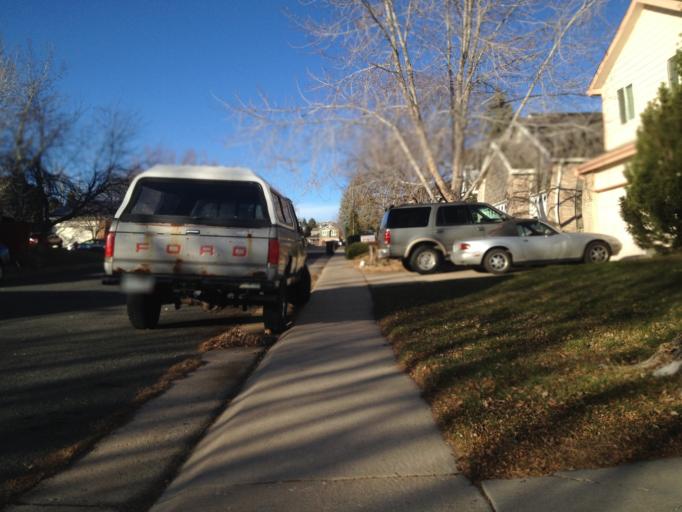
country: US
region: Colorado
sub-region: Boulder County
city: Superior
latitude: 39.9700
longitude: -105.1607
